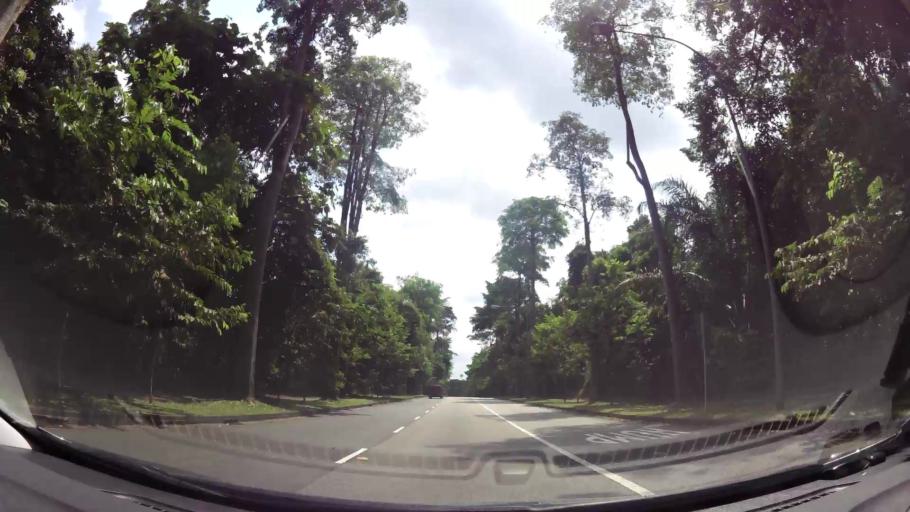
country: MY
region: Johor
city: Johor Bahru
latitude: 1.4062
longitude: 103.7853
